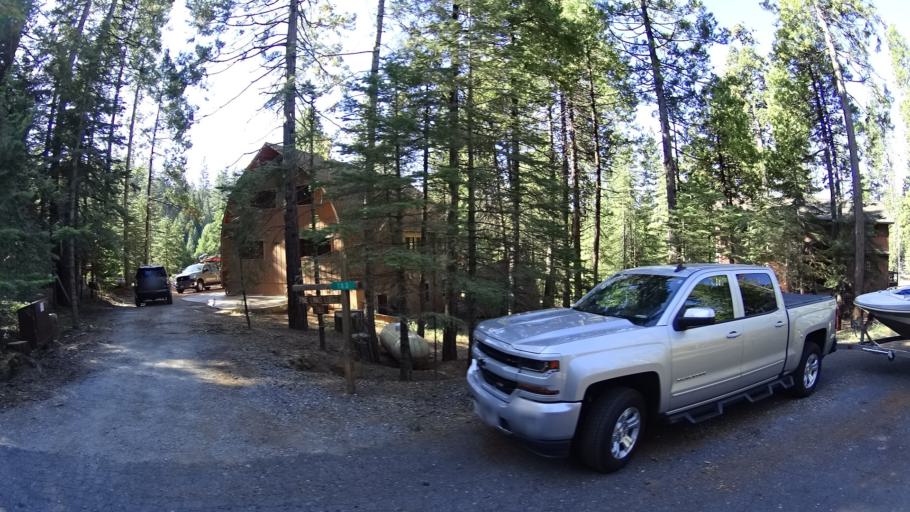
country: US
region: California
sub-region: Calaveras County
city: Arnold
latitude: 38.2581
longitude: -120.3266
